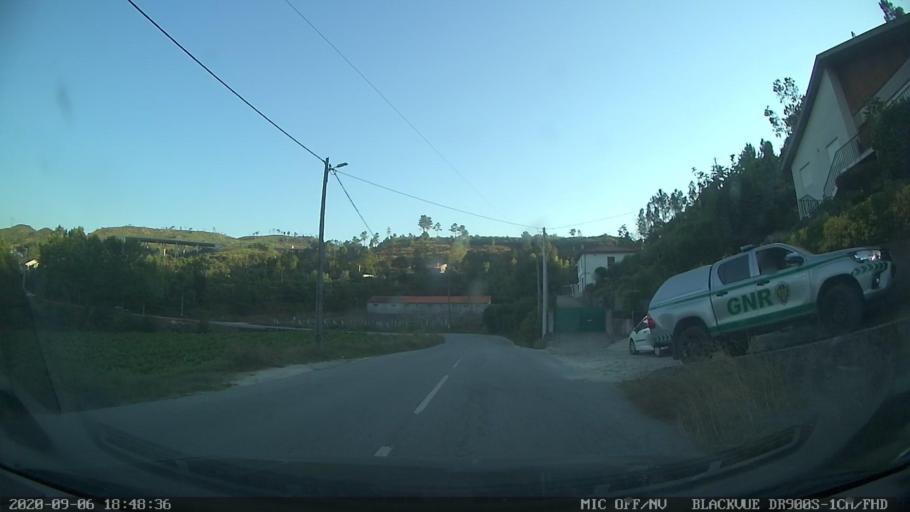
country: PT
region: Porto
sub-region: Amarante
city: Amarante
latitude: 41.2641
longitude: -8.0048
